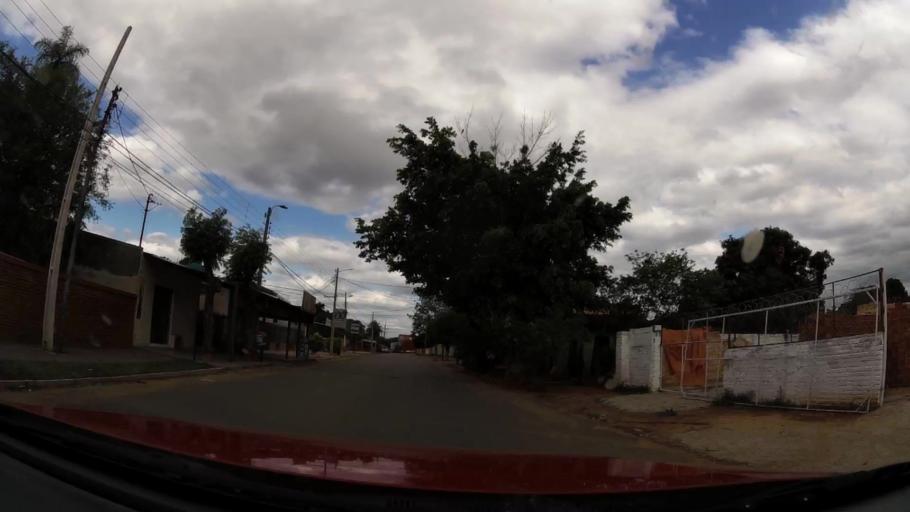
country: PY
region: Central
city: San Lorenzo
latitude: -25.2701
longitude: -57.5040
